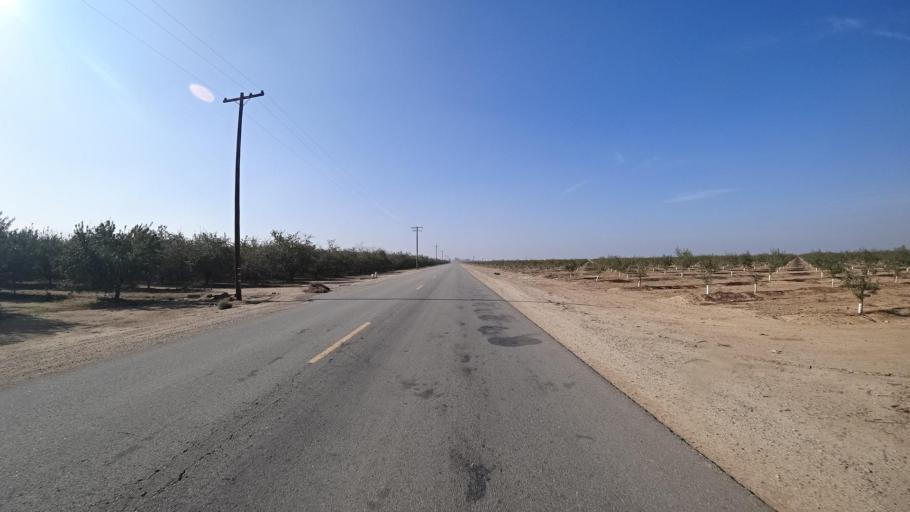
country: US
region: California
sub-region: Kern County
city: Shafter
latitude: 35.5296
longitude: -119.1704
